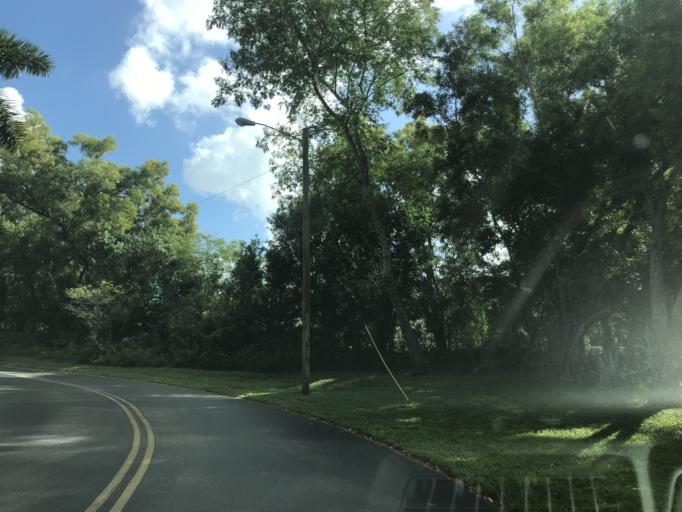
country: US
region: Florida
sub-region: Broward County
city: Margate
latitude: 26.2638
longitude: -80.1988
